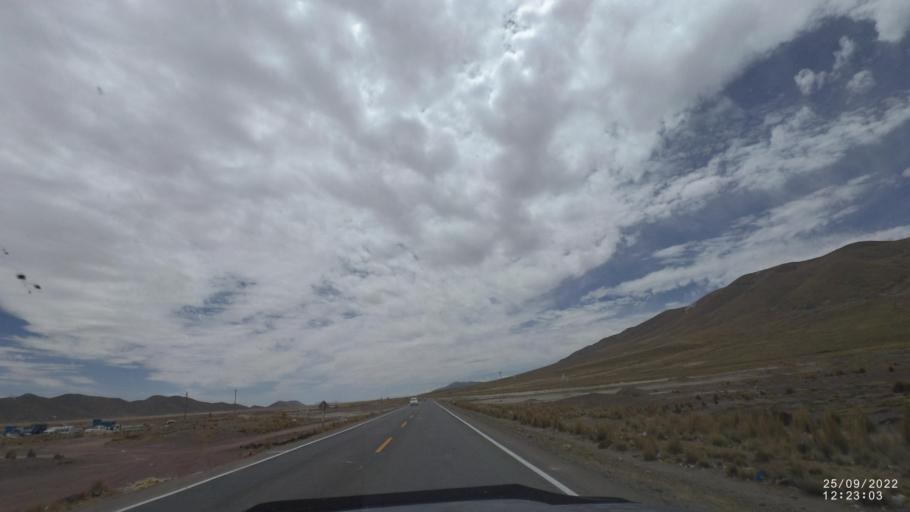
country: BO
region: Oruro
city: Poopo
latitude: -18.3799
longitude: -66.9795
